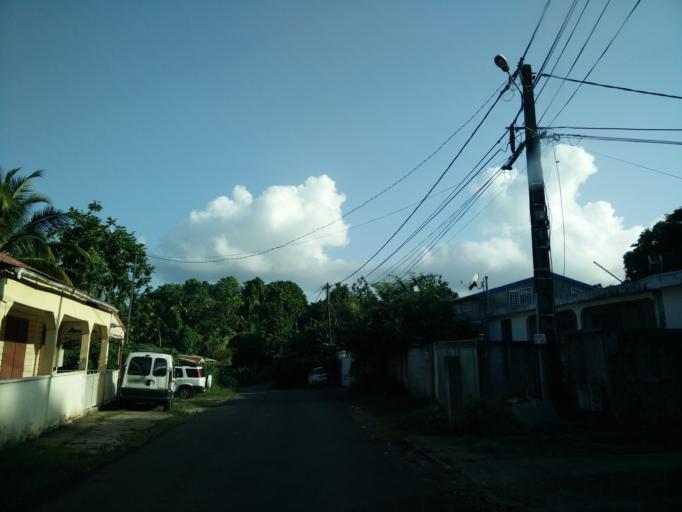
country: GP
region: Guadeloupe
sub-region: Guadeloupe
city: Pointe-a-Pitre
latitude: 16.2451
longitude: -61.5140
